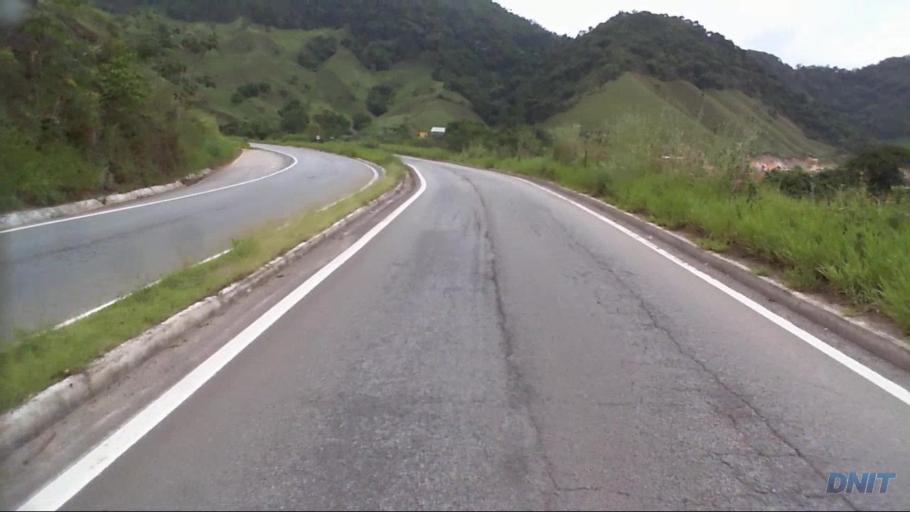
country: BR
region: Minas Gerais
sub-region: Timoteo
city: Timoteo
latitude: -19.6187
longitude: -42.8469
